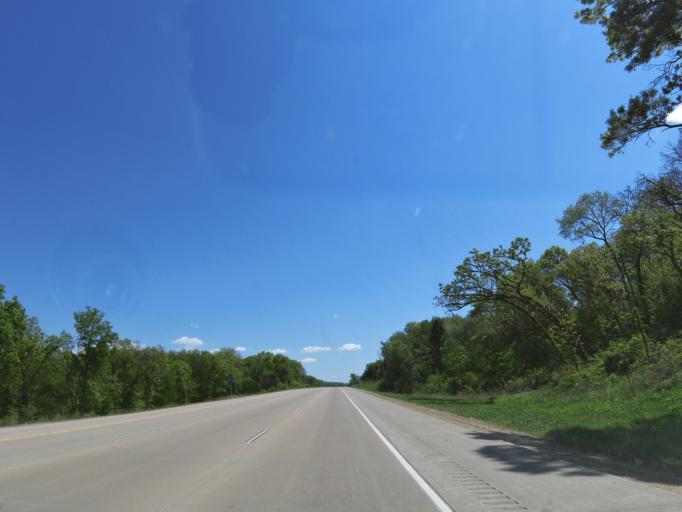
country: US
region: Wisconsin
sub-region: Columbia County
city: Poynette
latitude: 43.3837
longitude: -89.4647
